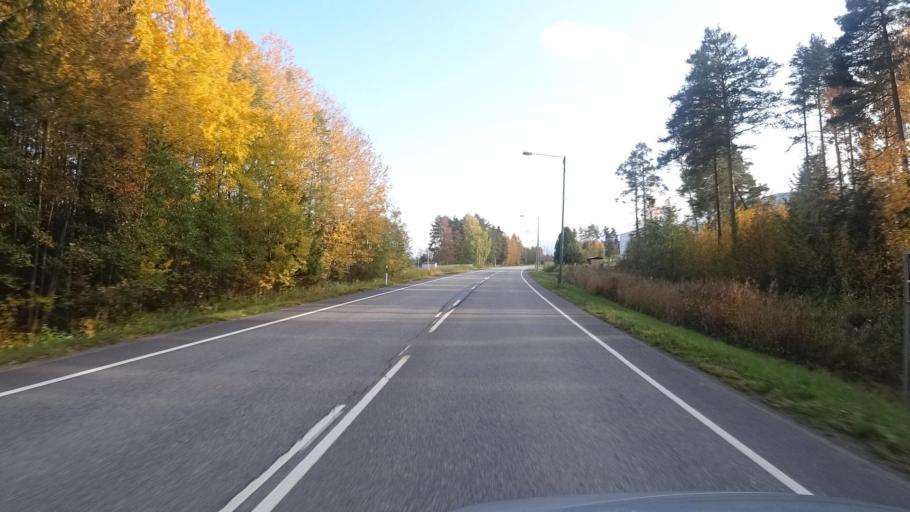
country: FI
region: Satakunta
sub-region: Rauma
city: Saekylae
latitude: 61.0650
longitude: 22.3230
